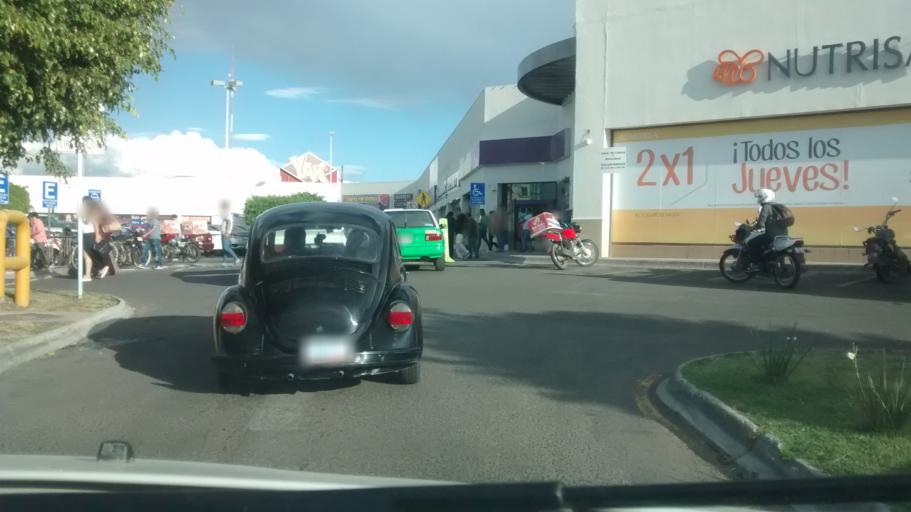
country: MX
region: Guanajuato
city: Leon
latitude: 21.1002
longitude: -101.6372
